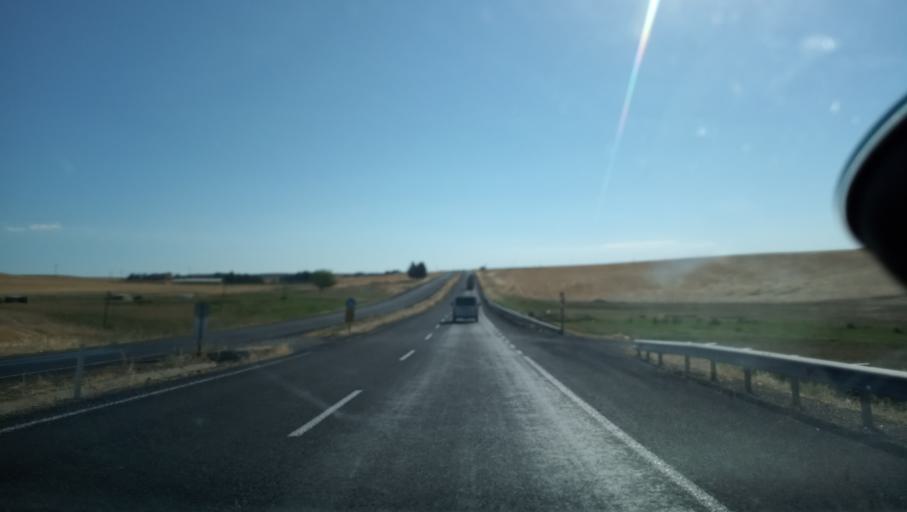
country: TR
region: Diyarbakir
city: Ambar
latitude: 37.9958
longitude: 40.4057
